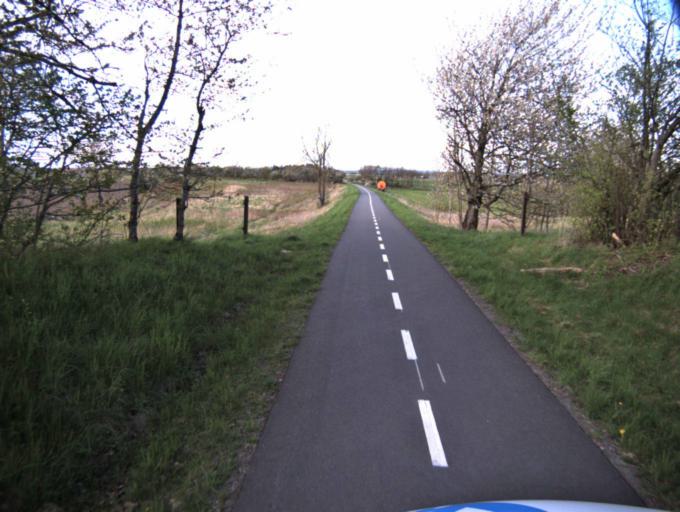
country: SE
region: Skane
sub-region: Kristianstads Kommun
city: Kristianstad
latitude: 56.0113
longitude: 14.0819
